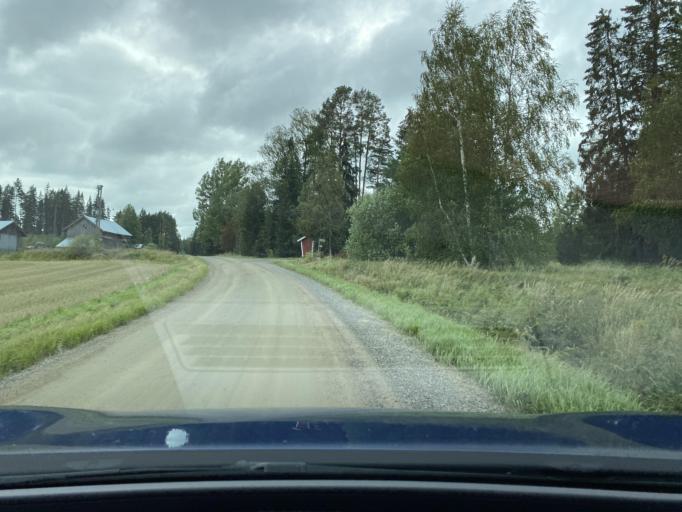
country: FI
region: Pirkanmaa
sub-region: Lounais-Pirkanmaa
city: Punkalaidun
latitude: 61.1806
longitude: 23.1825
